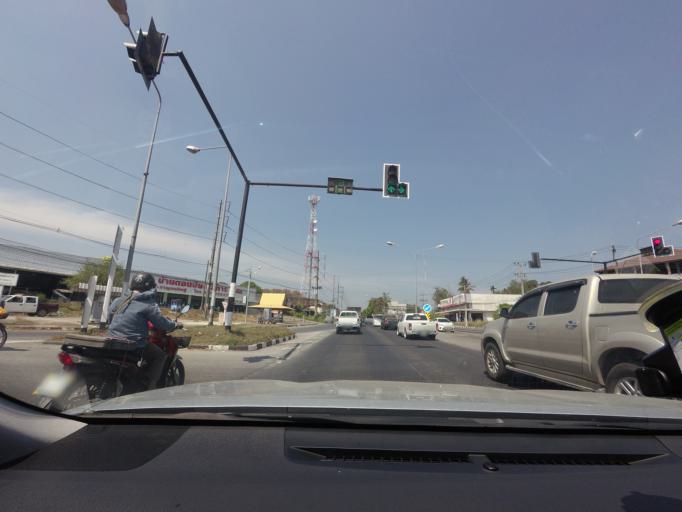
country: TH
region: Surat Thani
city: Kanchanadit
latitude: 9.1624
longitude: 99.4796
